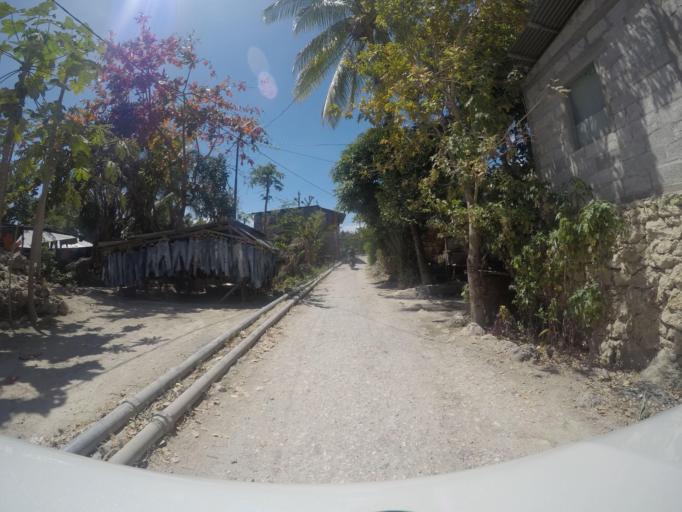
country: TL
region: Baucau
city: Baucau
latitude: -8.4671
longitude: 126.4585
